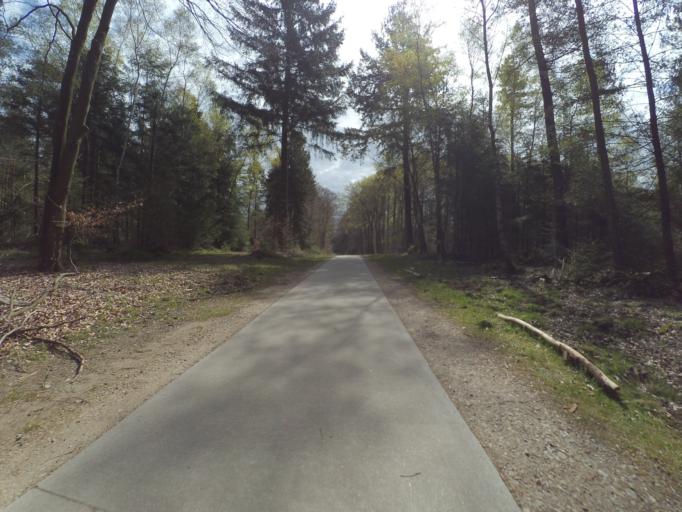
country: NL
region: Gelderland
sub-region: Gemeente Epe
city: Epe
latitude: 52.3751
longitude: 5.9604
